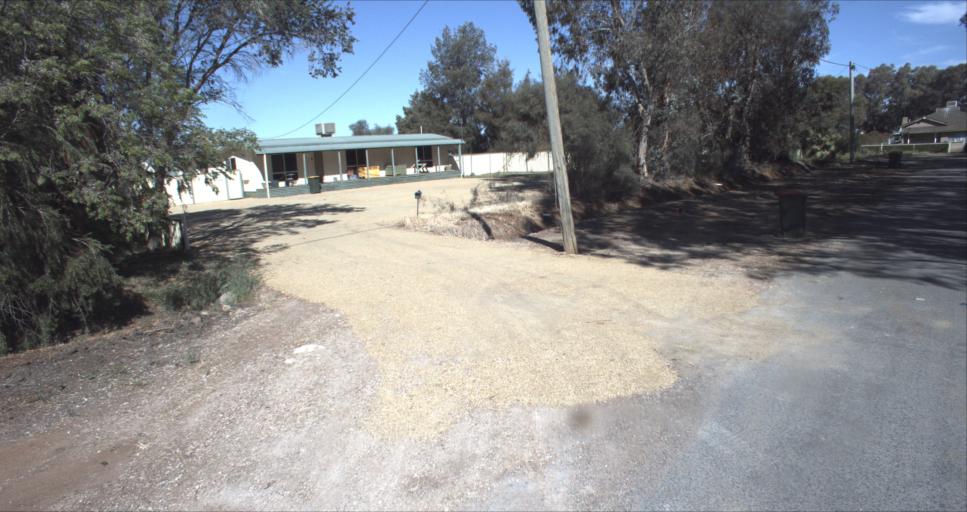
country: AU
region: New South Wales
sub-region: Leeton
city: Leeton
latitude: -34.5595
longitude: 146.3884
